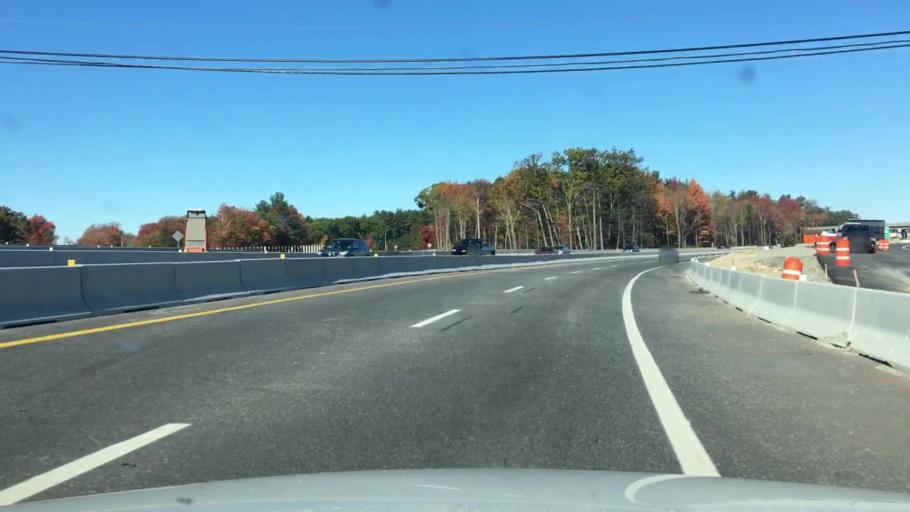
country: US
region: Maine
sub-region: York County
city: Eliot
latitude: 43.1262
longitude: -70.8367
